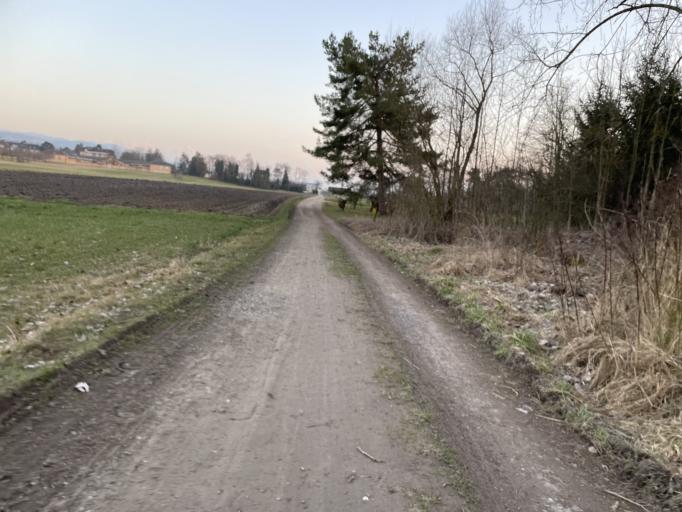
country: CH
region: Bern
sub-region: Bern-Mittelland District
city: Rubigen
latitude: 46.8839
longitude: 7.5463
